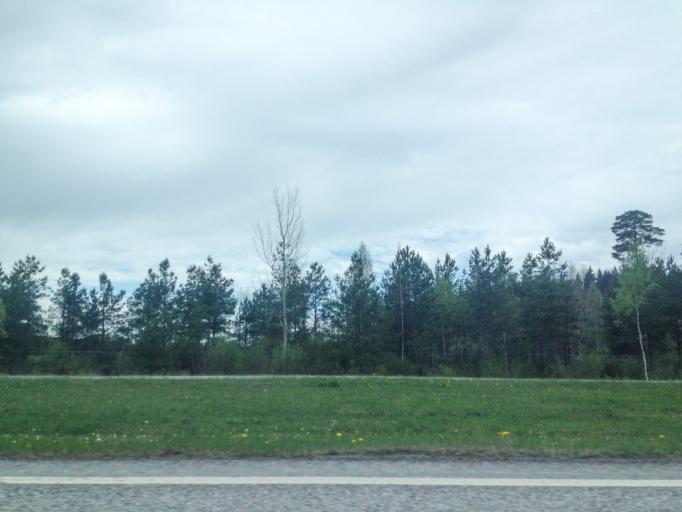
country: FI
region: Uusimaa
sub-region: Helsinki
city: Nurmijaervi
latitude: 60.5140
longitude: 24.8475
